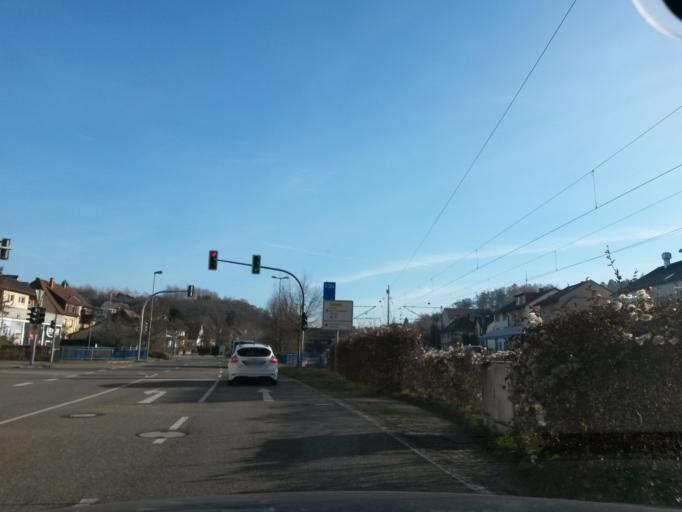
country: DE
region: Baden-Wuerttemberg
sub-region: Karlsruhe Region
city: Ispringen
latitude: 48.9150
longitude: 8.6712
